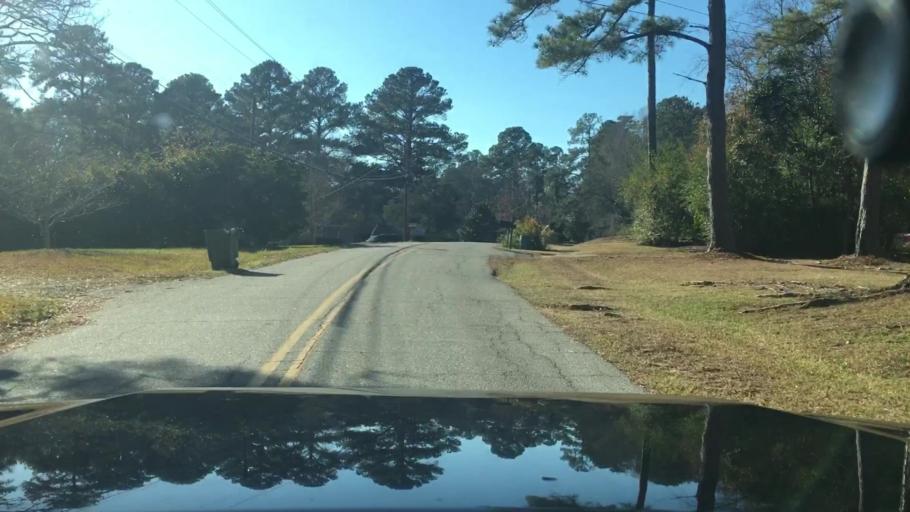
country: US
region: Georgia
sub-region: Bibb County
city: Macon
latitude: 32.8802
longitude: -83.6821
